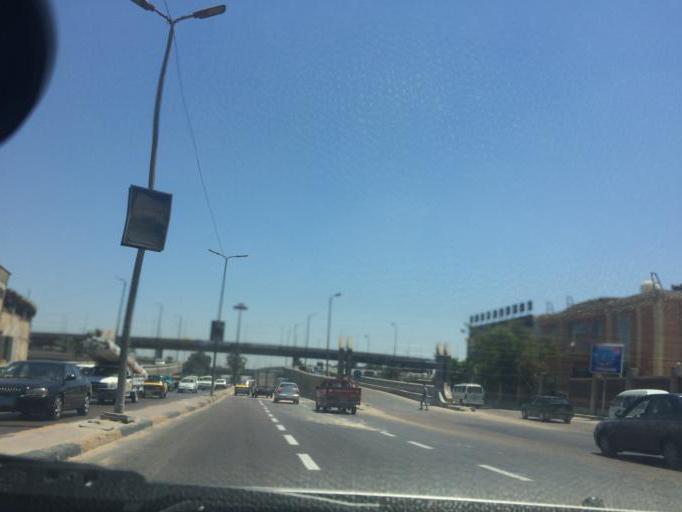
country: EG
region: Alexandria
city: Alexandria
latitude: 31.1834
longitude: 29.9268
